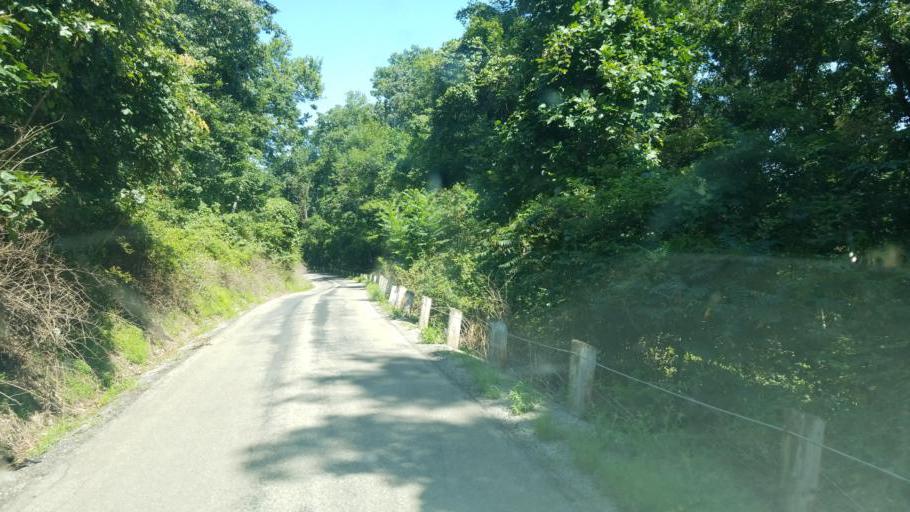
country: US
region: Pennsylvania
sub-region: Clarion County
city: Clarion
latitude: 41.1811
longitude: -79.4318
